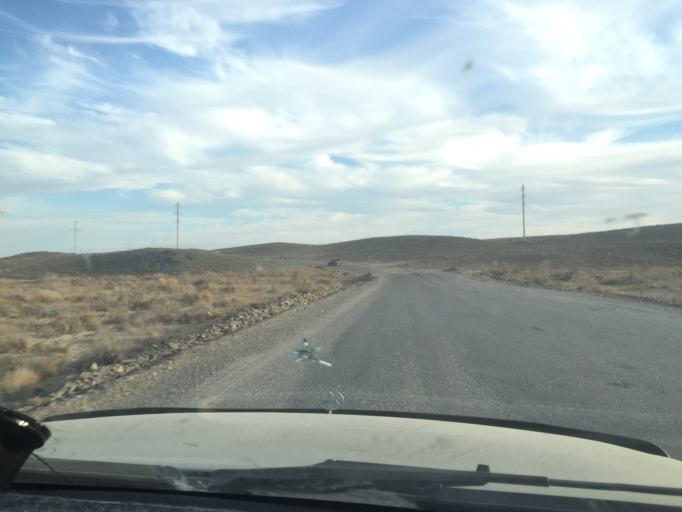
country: KZ
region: Almaty Oblysy
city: Ulken
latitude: 45.2073
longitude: 73.8802
